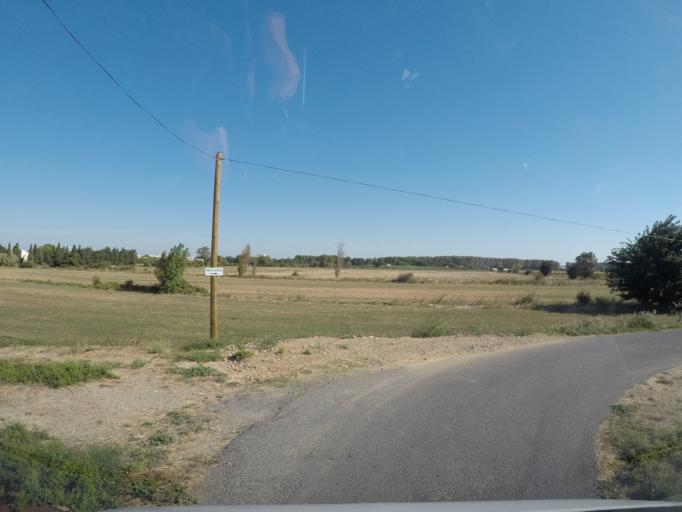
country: FR
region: Languedoc-Roussillon
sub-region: Departement de l'Aude
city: Narbonne
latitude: 43.1713
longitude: 3.0118
